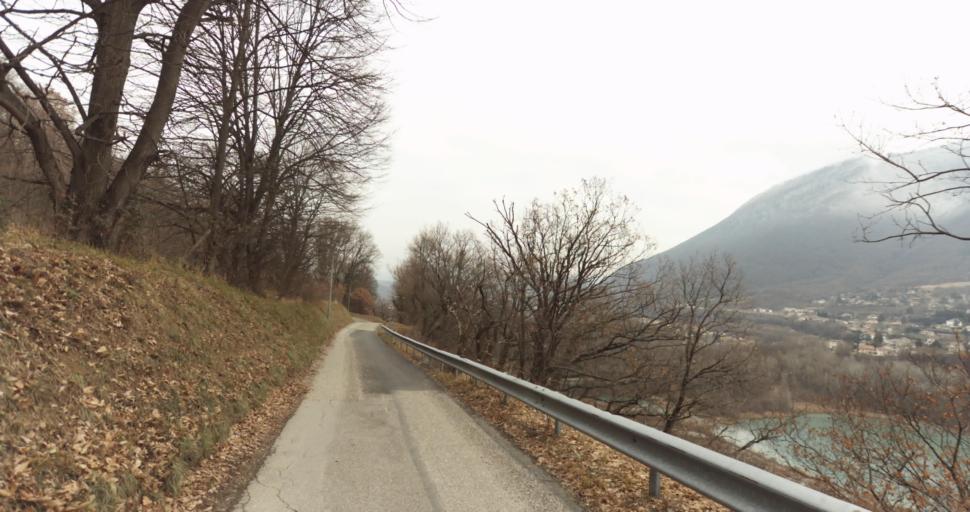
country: FR
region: Rhone-Alpes
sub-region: Departement de l'Isere
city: Saint-Georges-de-Commiers
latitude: 45.0416
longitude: 5.6925
